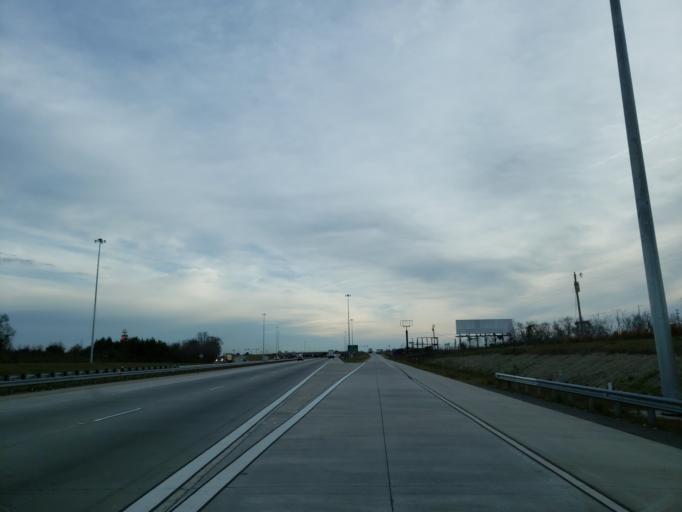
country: US
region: Georgia
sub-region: Dooly County
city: Vienna
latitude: 32.0912
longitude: -83.7635
